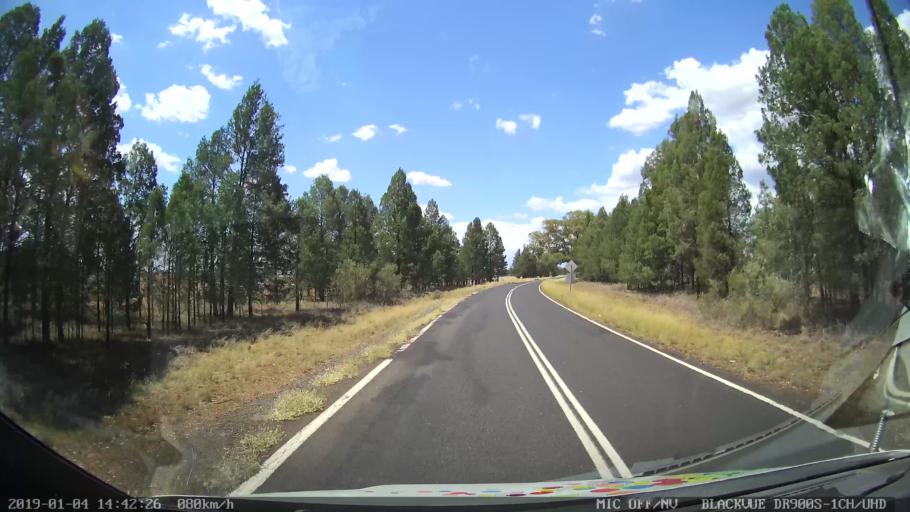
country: AU
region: New South Wales
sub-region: Dubbo Municipality
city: Dubbo
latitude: -32.1280
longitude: 148.6419
